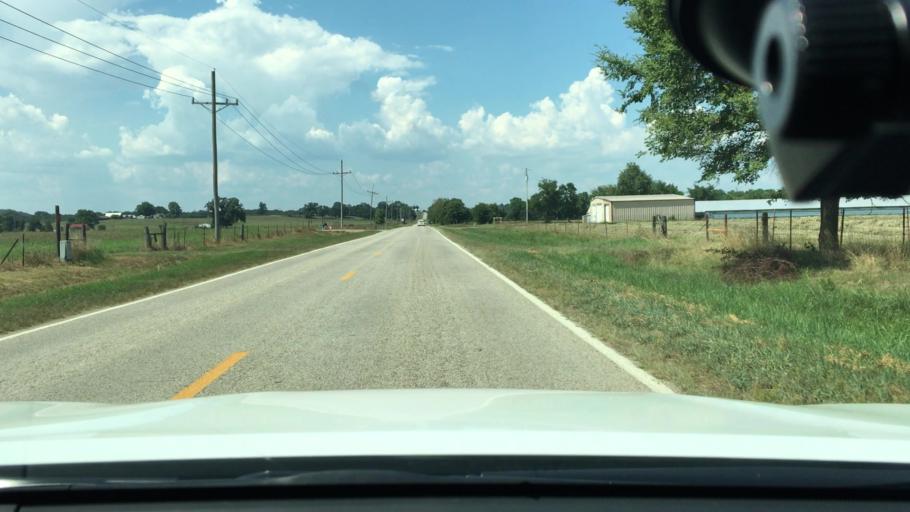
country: US
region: Arkansas
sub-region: Logan County
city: Paris
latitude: 35.3278
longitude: -93.6321
